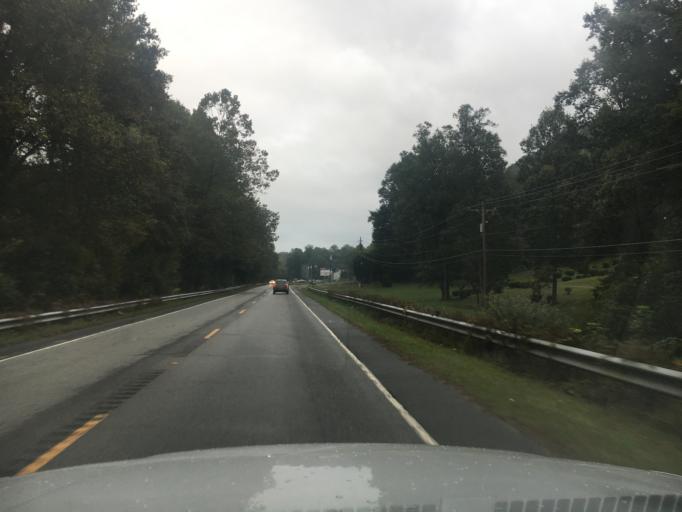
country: US
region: North Carolina
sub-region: Henderson County
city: Horse Shoe
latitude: 35.3339
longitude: -82.5697
